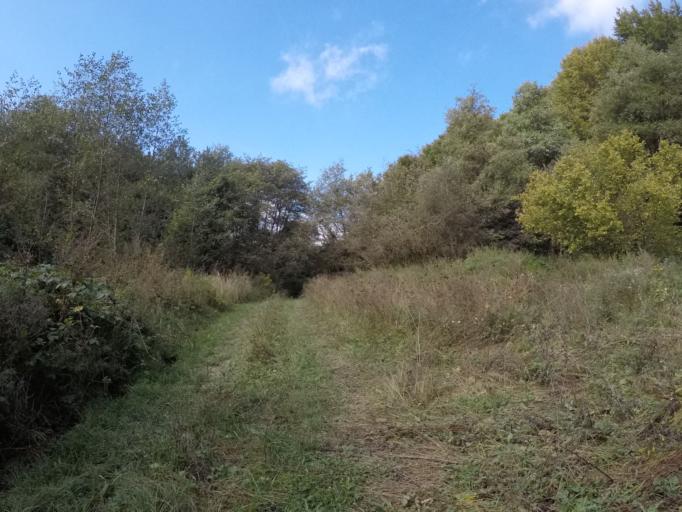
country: SK
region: Presovsky
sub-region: Okres Presov
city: Presov
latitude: 48.9329
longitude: 21.1645
